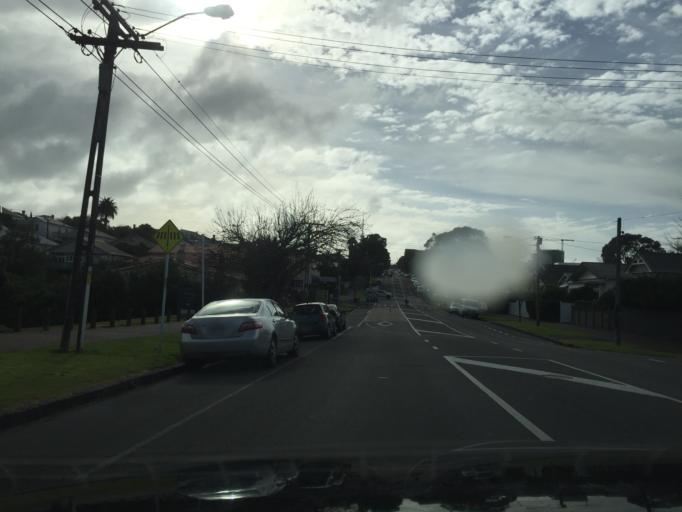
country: NZ
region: Auckland
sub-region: Auckland
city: Auckland
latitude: -36.8620
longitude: 174.7425
